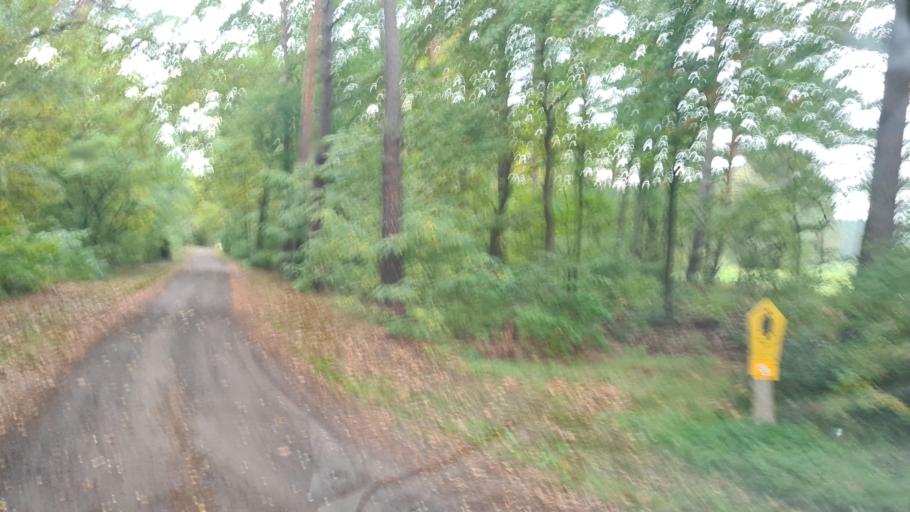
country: DE
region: Brandenburg
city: Storkow
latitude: 52.2249
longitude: 13.9346
